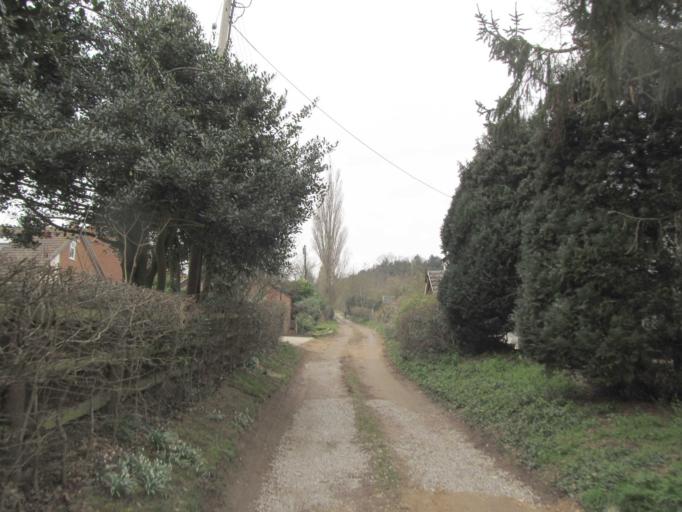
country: GB
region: England
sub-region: Doncaster
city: Bawtry
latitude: 53.4178
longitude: -0.9697
